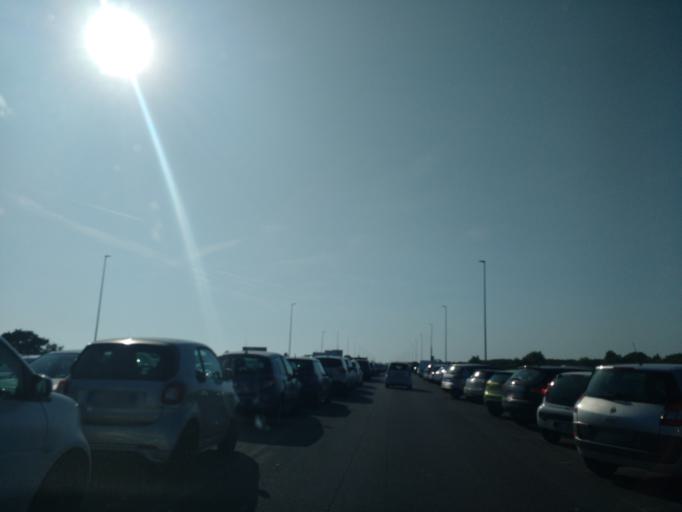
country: IT
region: Latium
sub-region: Citta metropolitana di Roma Capitale
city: Acilia-Castel Fusano-Ostia Antica
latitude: 41.7039
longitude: 12.3414
